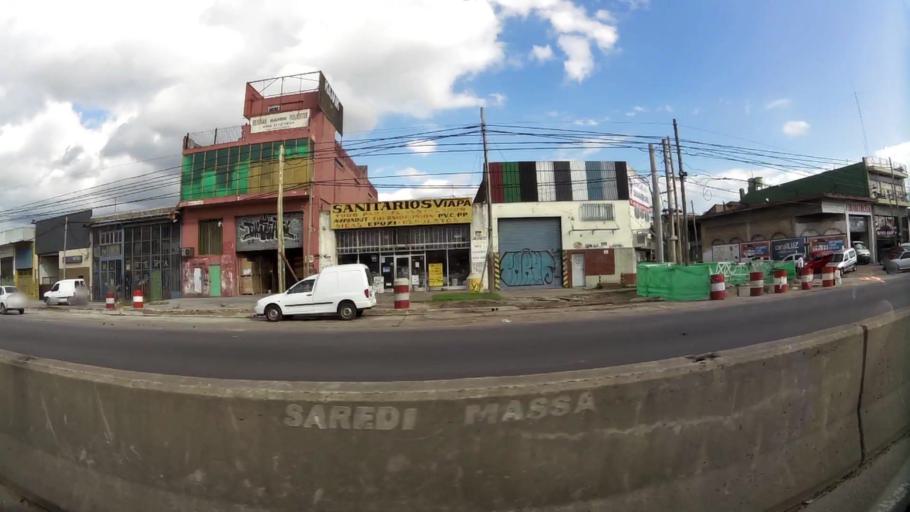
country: AR
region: Buenos Aires
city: San Justo
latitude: -34.6915
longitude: -58.5709
